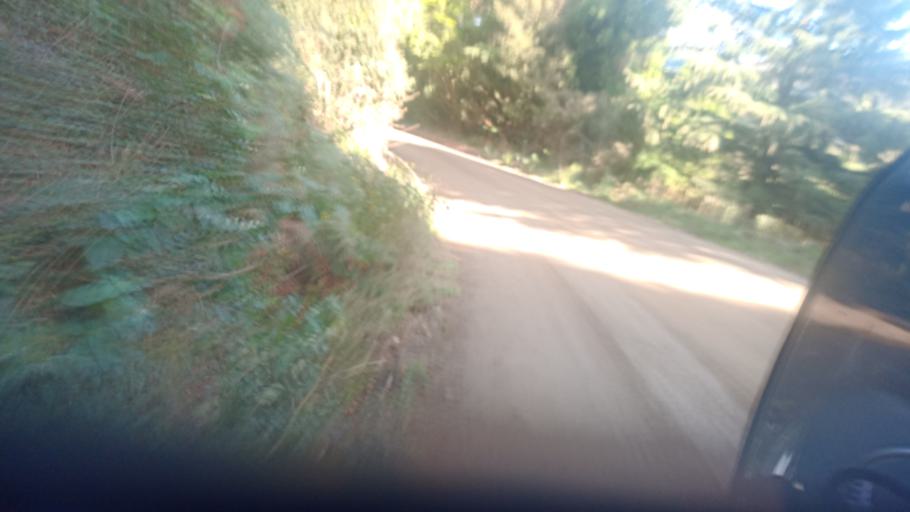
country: NZ
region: Bay of Plenty
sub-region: Opotiki District
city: Opotiki
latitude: -38.4350
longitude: 177.5483
